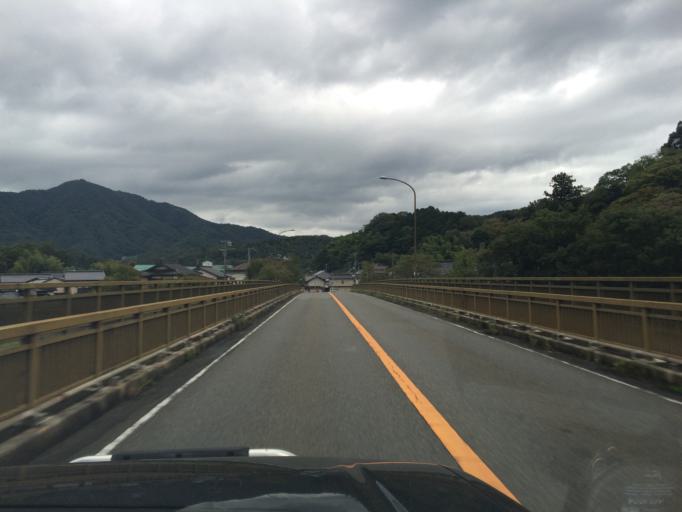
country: JP
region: Hyogo
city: Toyooka
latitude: 35.4274
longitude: 134.7933
